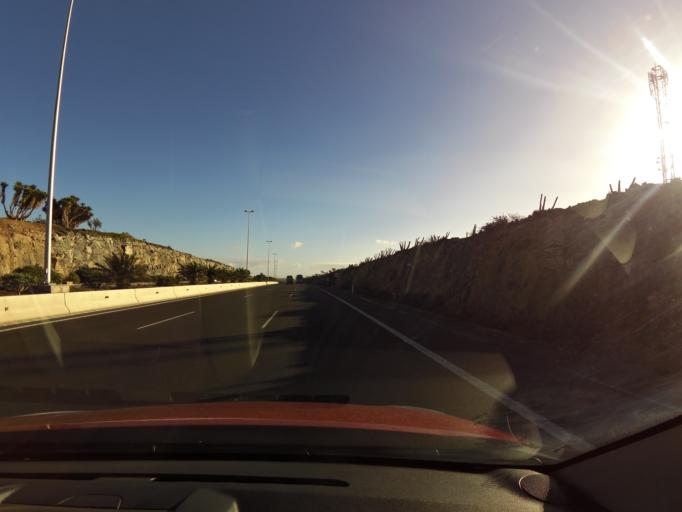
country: ES
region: Canary Islands
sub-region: Provincia de Las Palmas
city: Playa del Ingles
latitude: 27.7888
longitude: -15.5024
